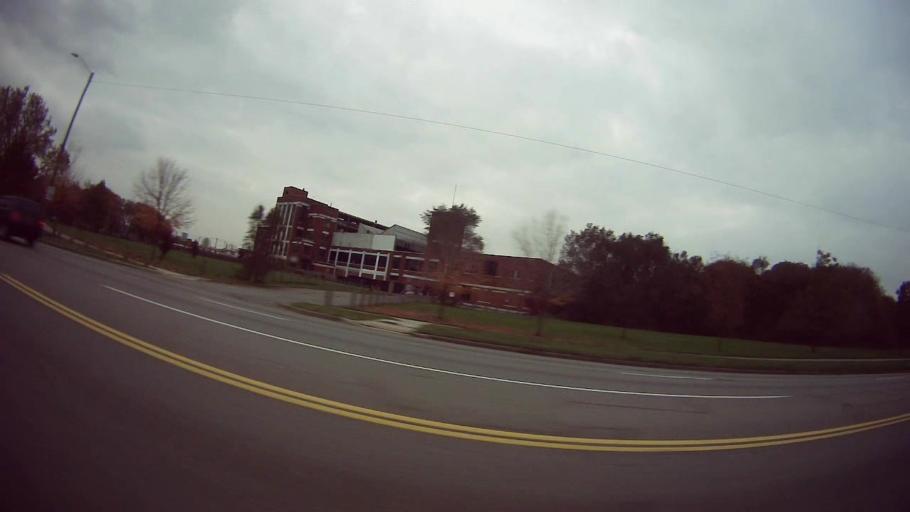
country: US
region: Michigan
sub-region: Wayne County
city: Hamtramck
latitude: 42.4008
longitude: -82.9928
